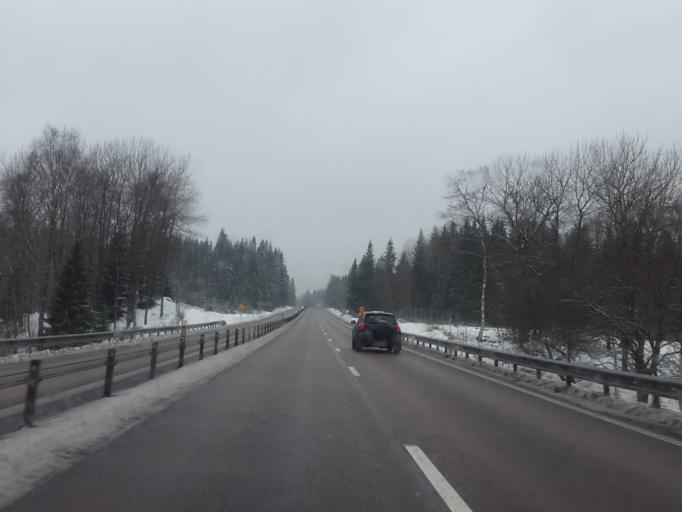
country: SE
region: Vaestra Goetaland
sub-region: Ulricehamns Kommun
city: Ulricehamn
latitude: 57.7975
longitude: 13.5356
